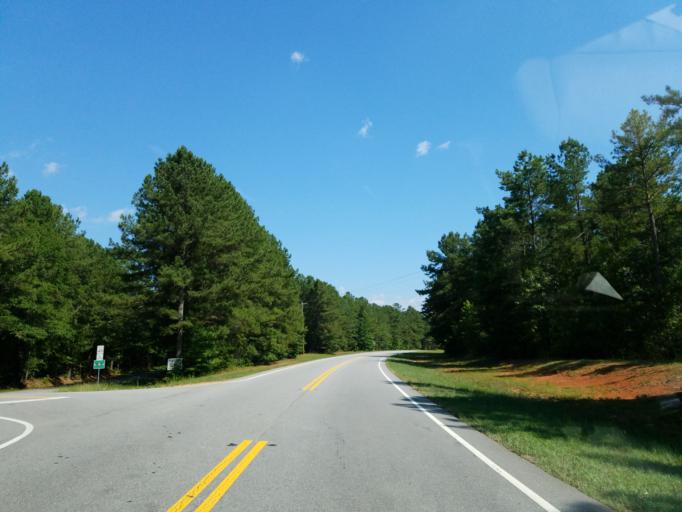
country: US
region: Georgia
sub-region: Lamar County
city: Barnesville
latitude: 32.9286
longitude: -84.0780
